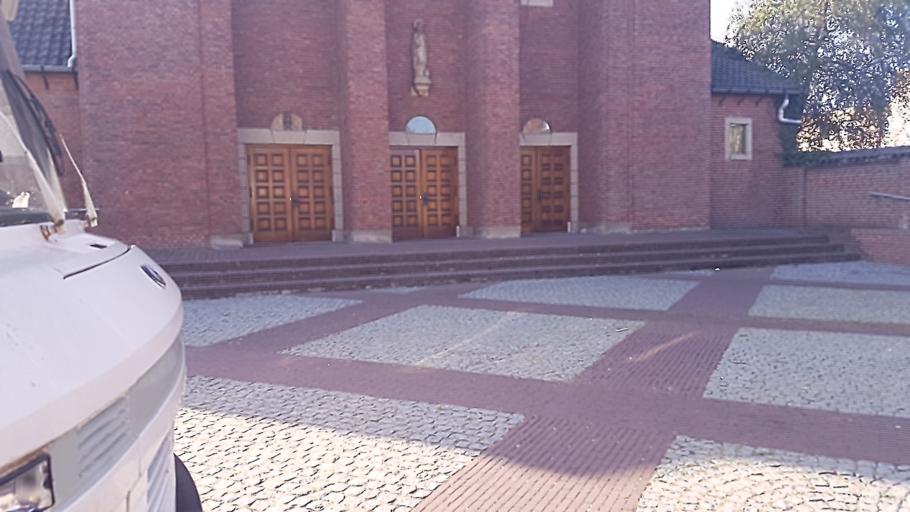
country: BE
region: Flanders
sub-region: Provincie Antwerpen
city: Stabroek
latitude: 51.3570
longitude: 4.3938
